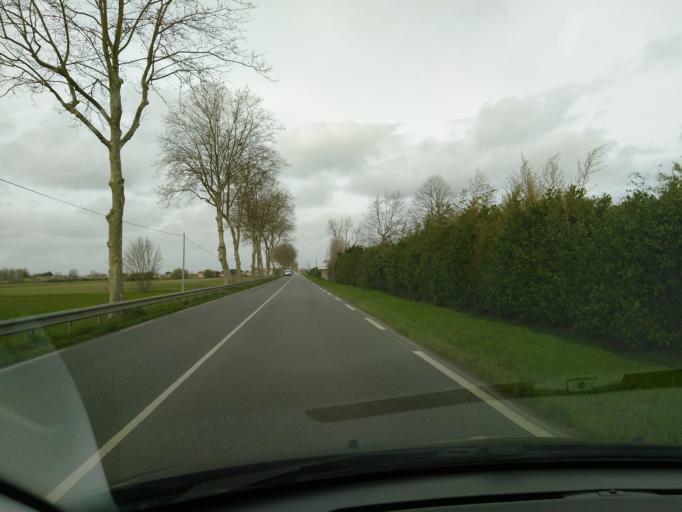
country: FR
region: Midi-Pyrenees
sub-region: Departement de la Haute-Garonne
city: Merville
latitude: 43.7324
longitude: 1.3189
